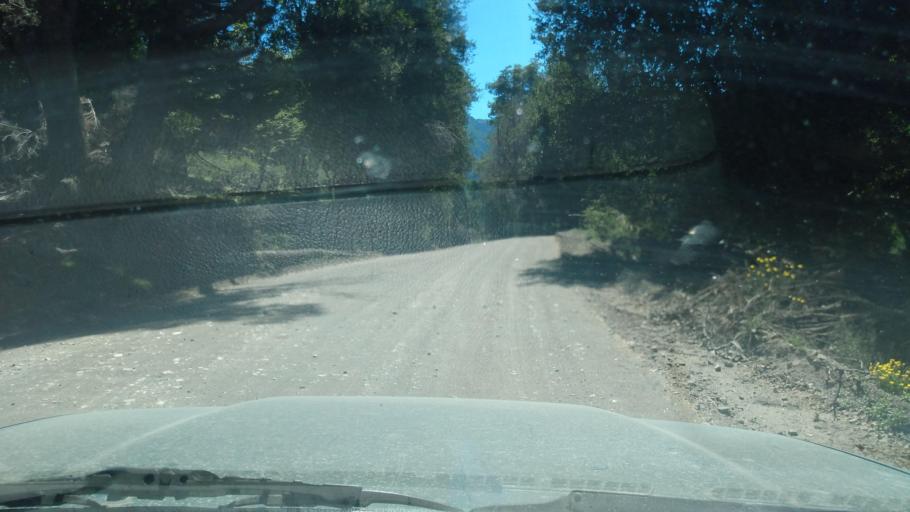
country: AR
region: Neuquen
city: Villa La Angostura
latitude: -40.6206
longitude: -71.5776
